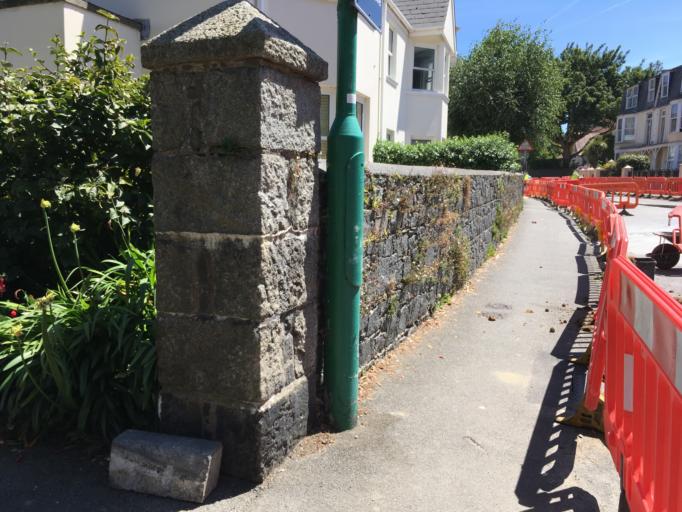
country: GG
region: St Peter Port
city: Saint Peter Port
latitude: 49.4604
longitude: -2.5457
